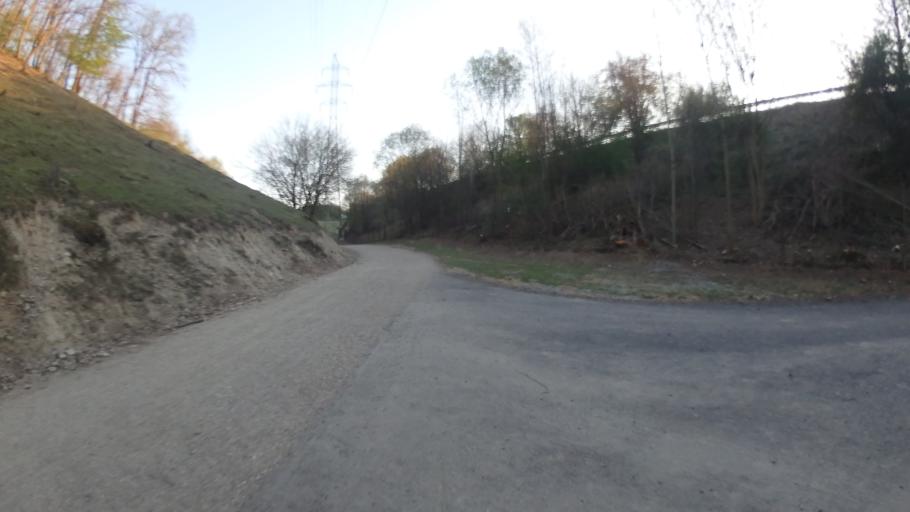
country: CZ
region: South Moravian
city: Troubsko
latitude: 49.2041
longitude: 16.5196
